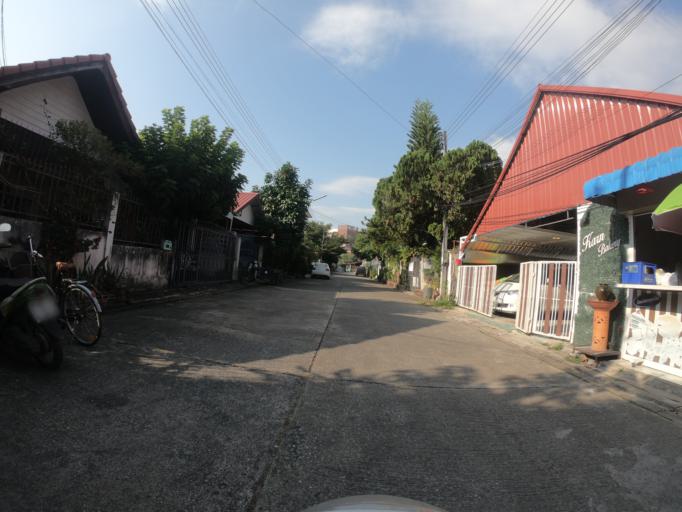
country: TH
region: Chiang Mai
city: Chiang Mai
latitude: 18.8010
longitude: 98.9924
